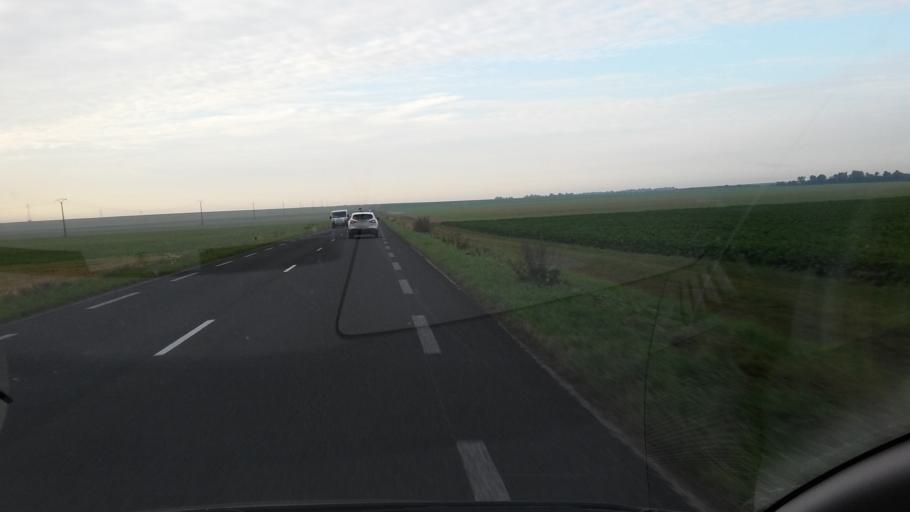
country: FR
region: Champagne-Ardenne
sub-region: Departement de la Marne
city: Fere-Champenoise
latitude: 48.8037
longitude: 3.9928
